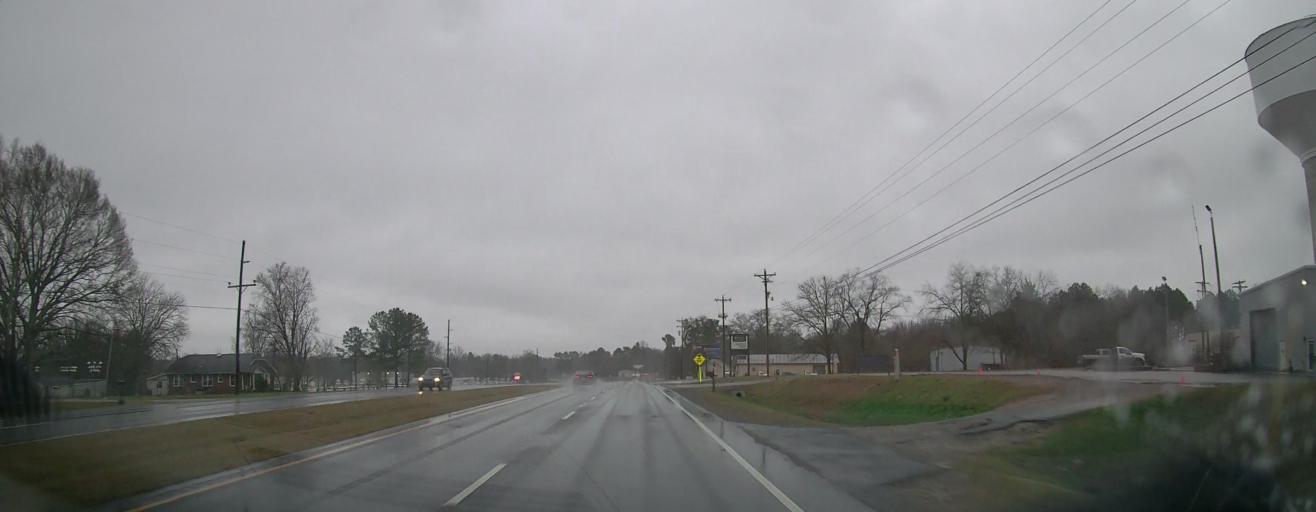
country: US
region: Alabama
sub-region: Morgan County
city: Hartselle
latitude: 34.4765
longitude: -86.9605
